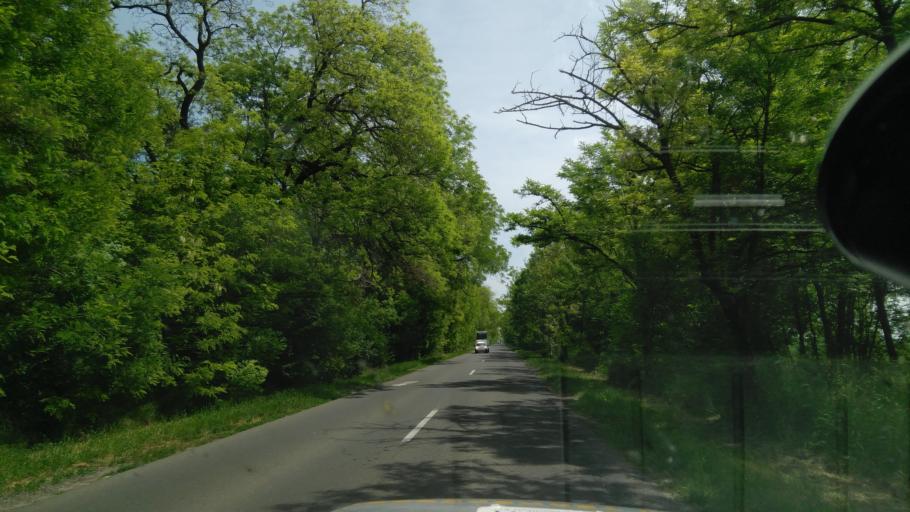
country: HU
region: Csongrad
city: Fabiansebestyen
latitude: 46.5755
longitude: 20.4479
